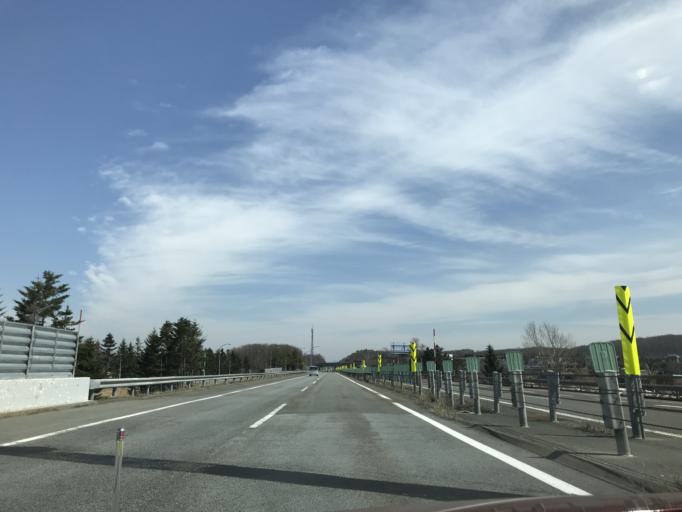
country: JP
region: Hokkaido
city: Iwamizawa
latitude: 43.1746
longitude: 141.7662
